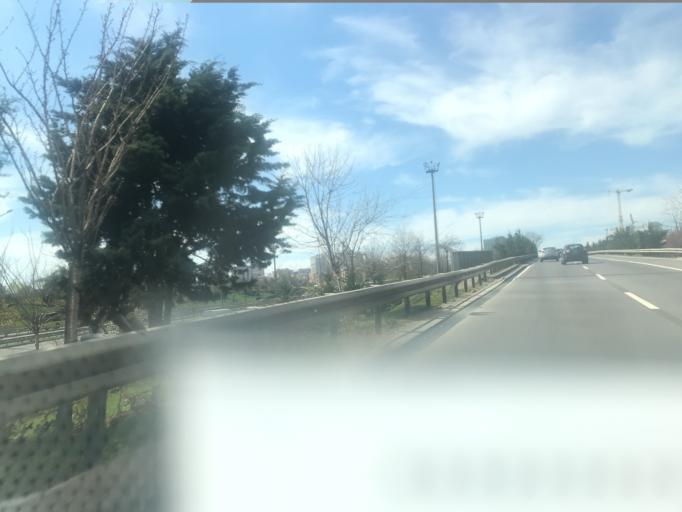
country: TR
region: Istanbul
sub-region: Atasehir
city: Atasehir
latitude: 40.9832
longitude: 29.1004
